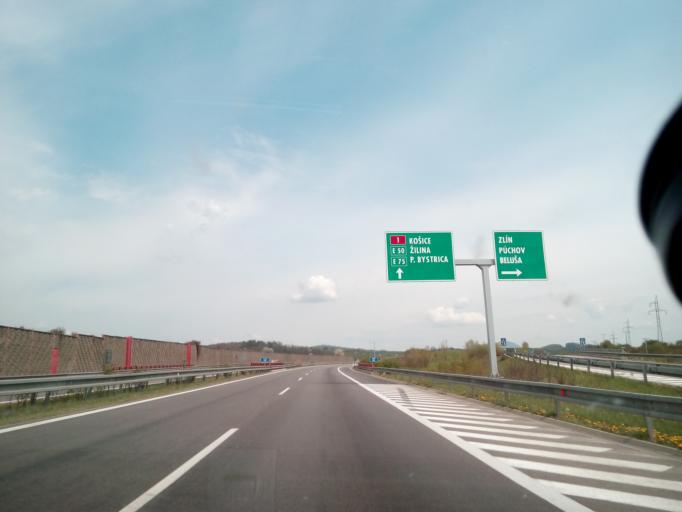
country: SK
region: Nitriansky
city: Puchov
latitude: 49.0598
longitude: 18.3339
